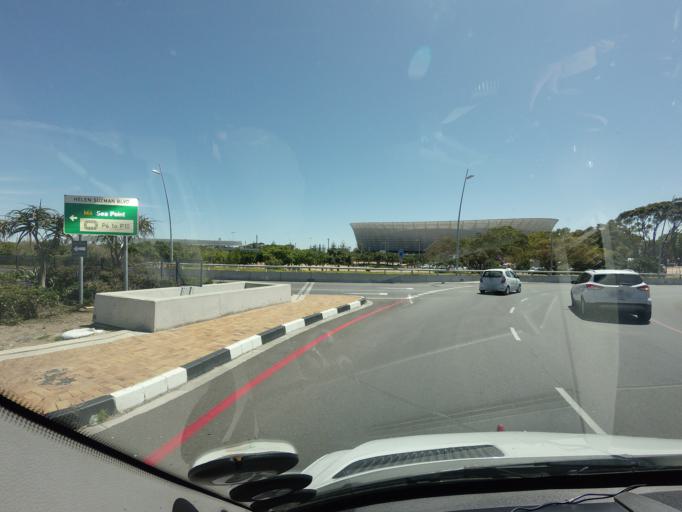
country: ZA
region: Western Cape
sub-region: City of Cape Town
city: Cape Town
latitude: -33.9076
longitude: 18.4094
